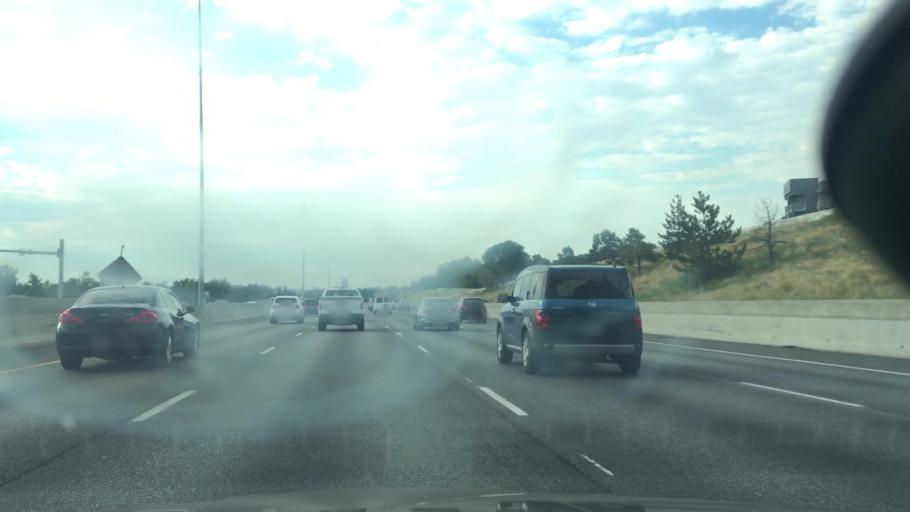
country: US
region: Colorado
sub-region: Arapahoe County
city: Cherry Hills Village
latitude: 39.6526
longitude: -104.9201
